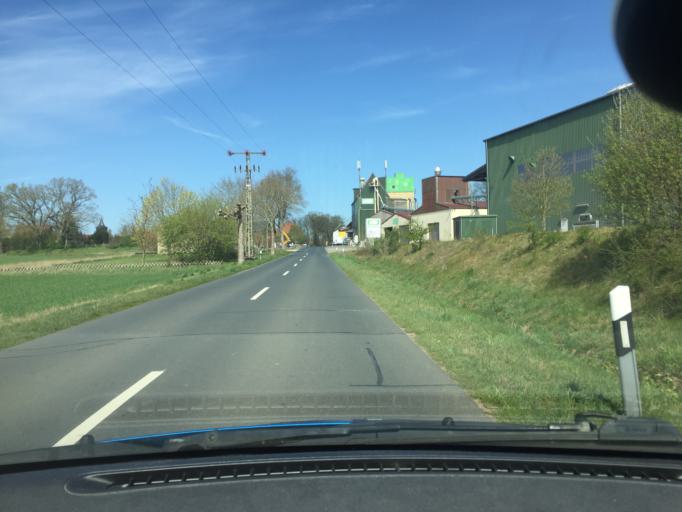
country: DE
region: Lower Saxony
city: Ratzlingen
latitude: 52.9724
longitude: 10.6779
